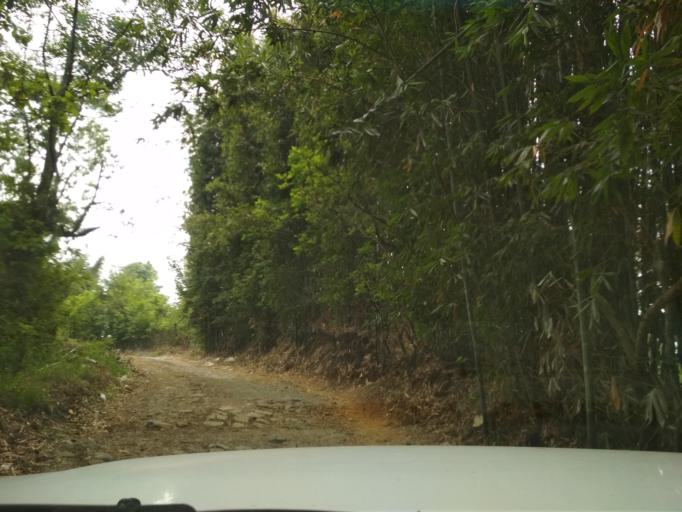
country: MX
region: Veracruz
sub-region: Mariano Escobedo
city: Mariano Escobedo
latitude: 18.9162
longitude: -97.1265
